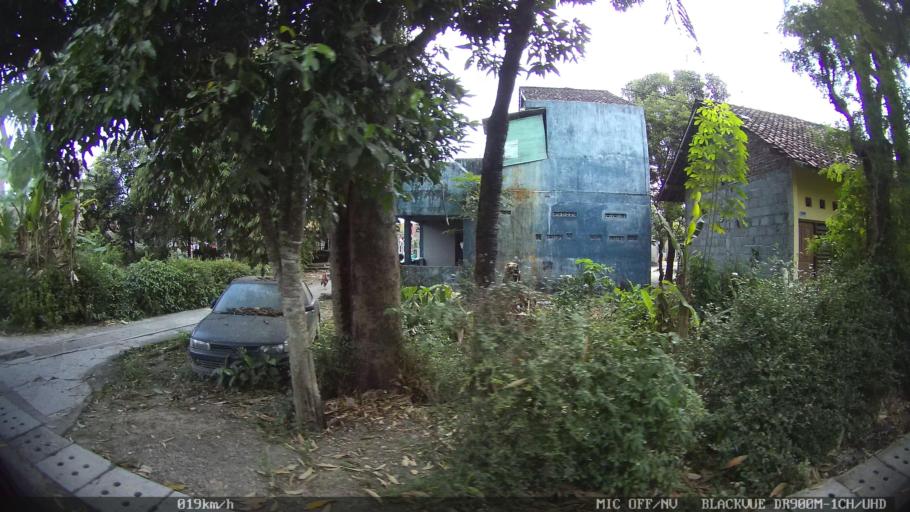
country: ID
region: Daerah Istimewa Yogyakarta
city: Kasihan
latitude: -7.8229
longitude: 110.3324
